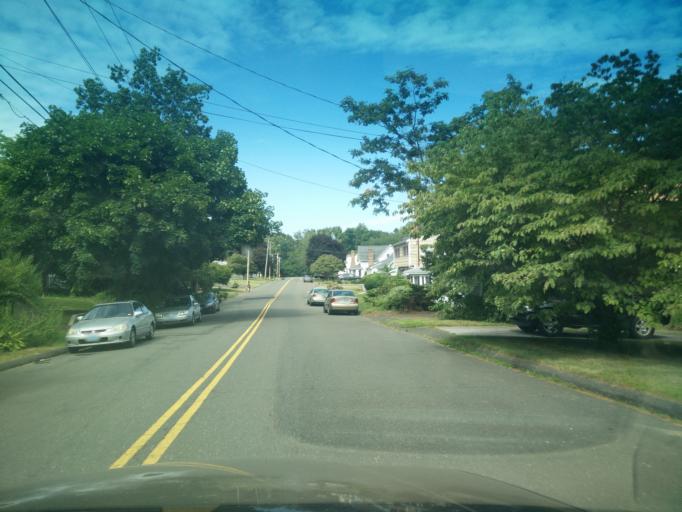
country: US
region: Connecticut
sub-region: Fairfield County
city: Bridgeport
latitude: 41.1816
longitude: -73.2311
